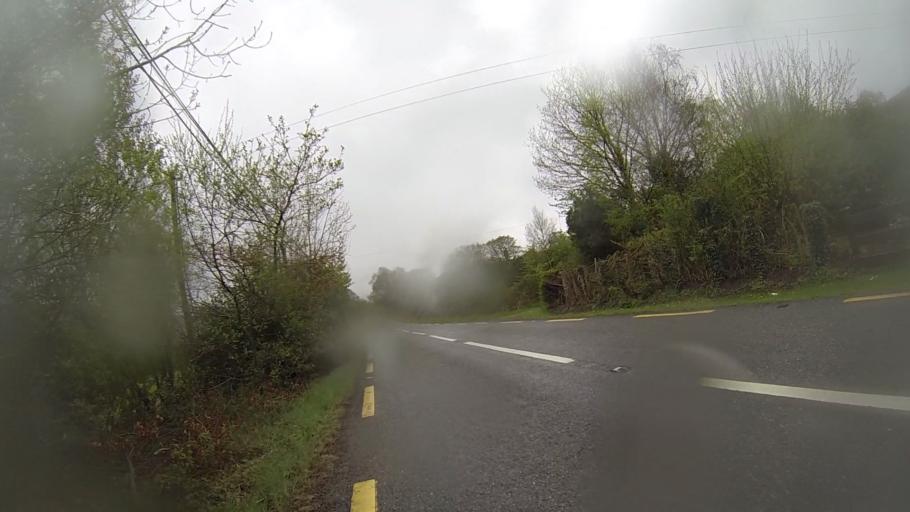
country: IE
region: Munster
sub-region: Ciarrai
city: Kenmare
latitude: 51.8192
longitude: -9.5309
